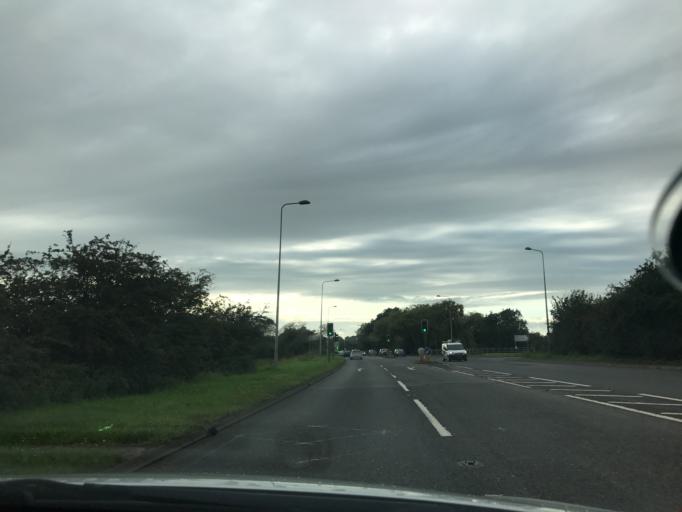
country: GB
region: England
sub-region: Cheshire West and Chester
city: Tarvin
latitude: 53.2000
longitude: -2.7971
